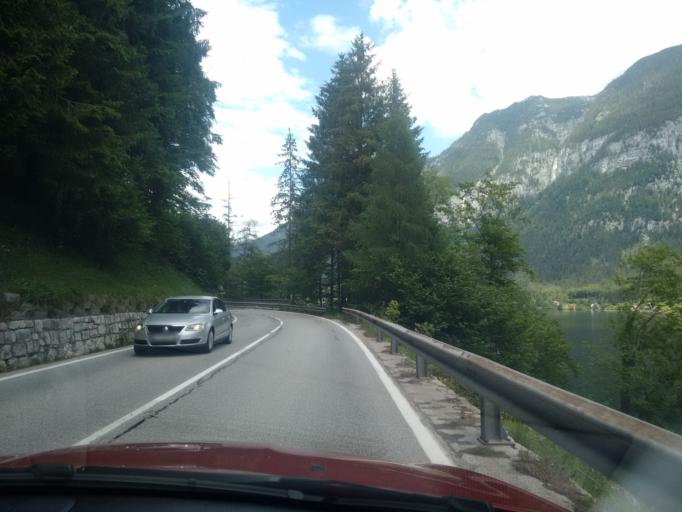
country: AT
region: Upper Austria
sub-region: Politischer Bezirk Gmunden
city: Bad Goisern
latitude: 47.5797
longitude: 13.6563
